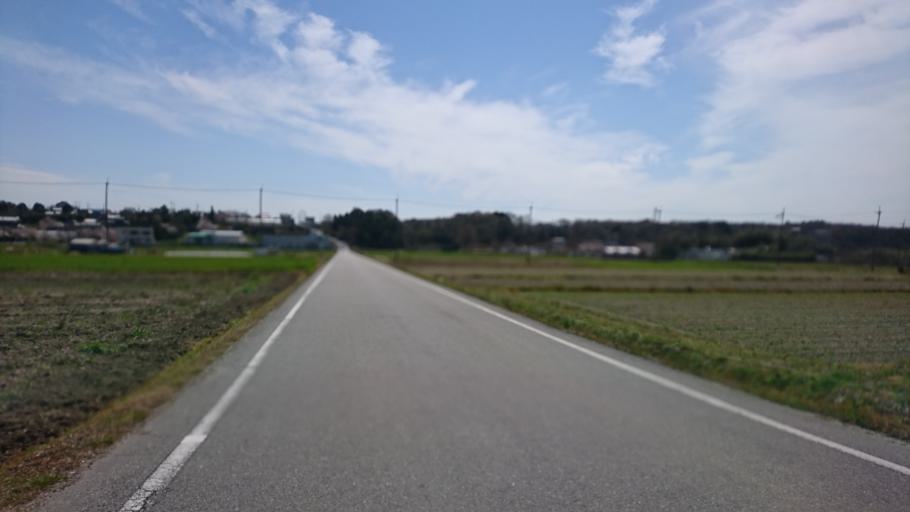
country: JP
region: Hyogo
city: Miki
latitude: 34.7748
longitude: 134.9376
